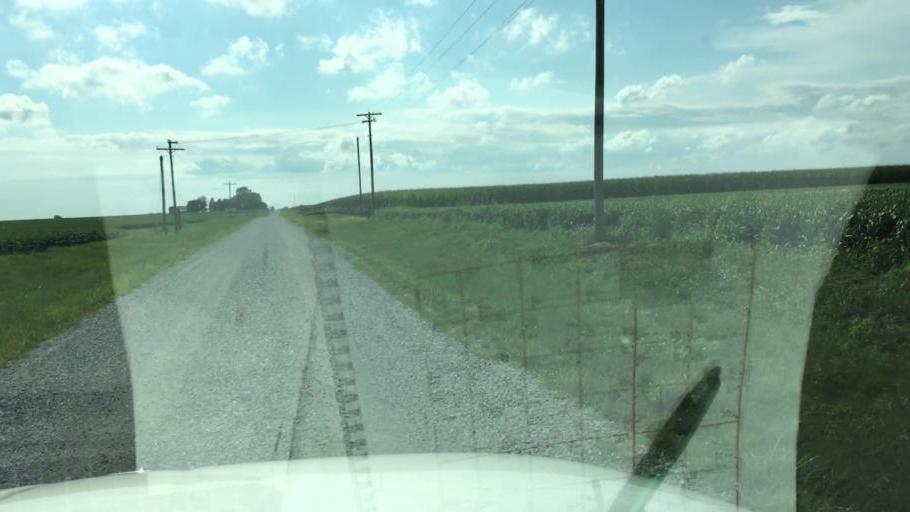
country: US
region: Illinois
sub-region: Hancock County
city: Nauvoo
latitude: 40.5214
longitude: -91.2827
